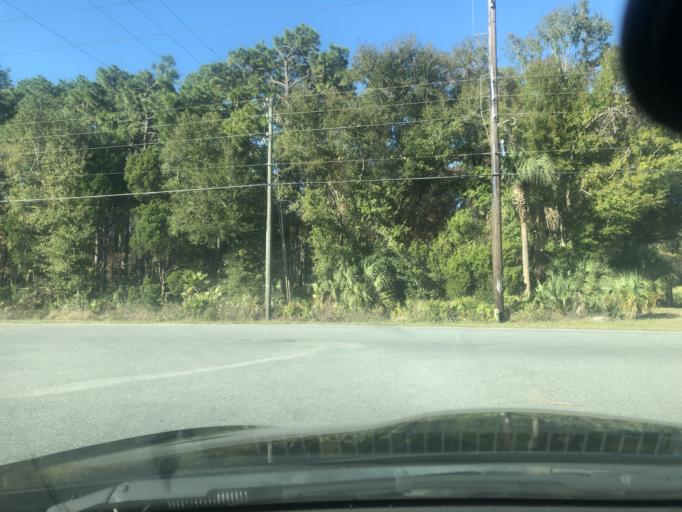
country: US
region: Florida
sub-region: Citrus County
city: Homosassa Springs
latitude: 28.8036
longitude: -82.5677
